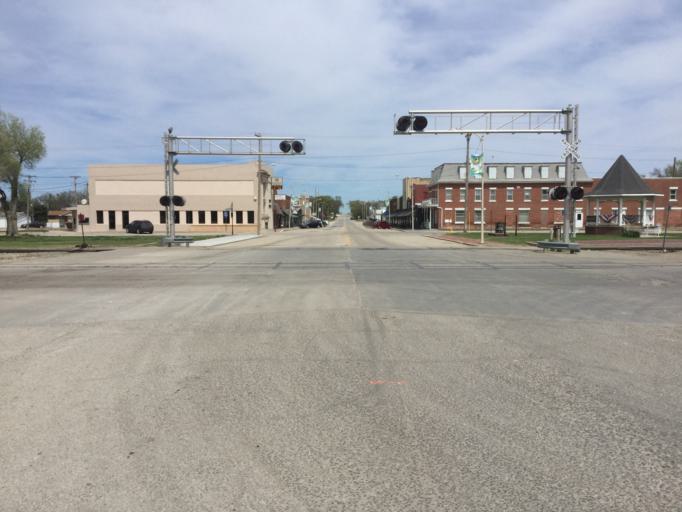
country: US
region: Kansas
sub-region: Osborne County
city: Osborne
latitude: 39.5020
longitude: -98.5444
